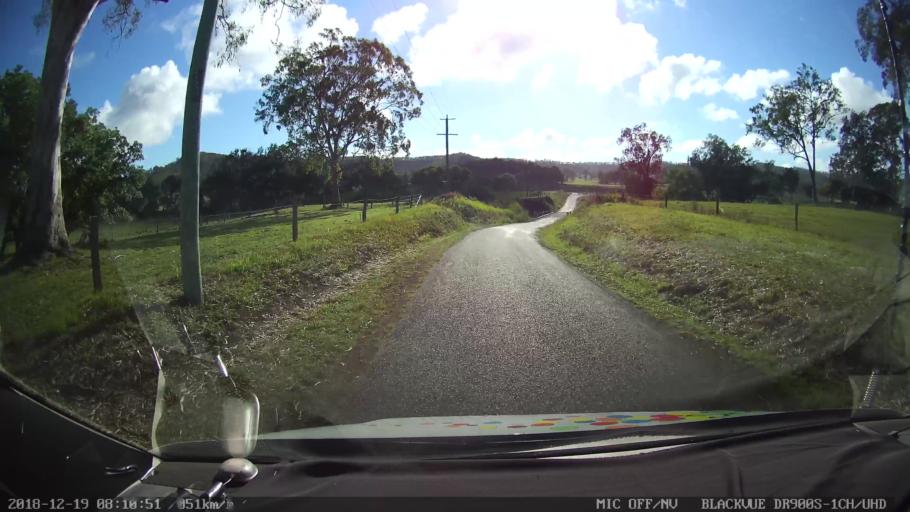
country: AU
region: Queensland
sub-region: Logan
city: Cedar Vale
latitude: -28.2165
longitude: 152.8893
